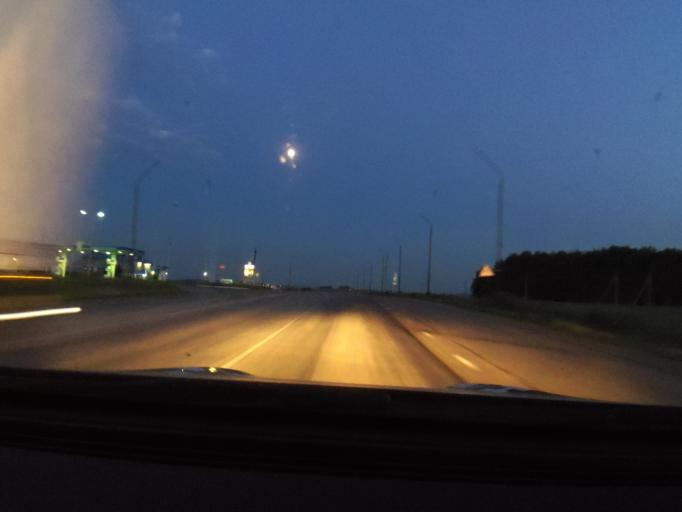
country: RU
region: Bashkortostan
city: Duvan
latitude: 55.9506
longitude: 58.1970
